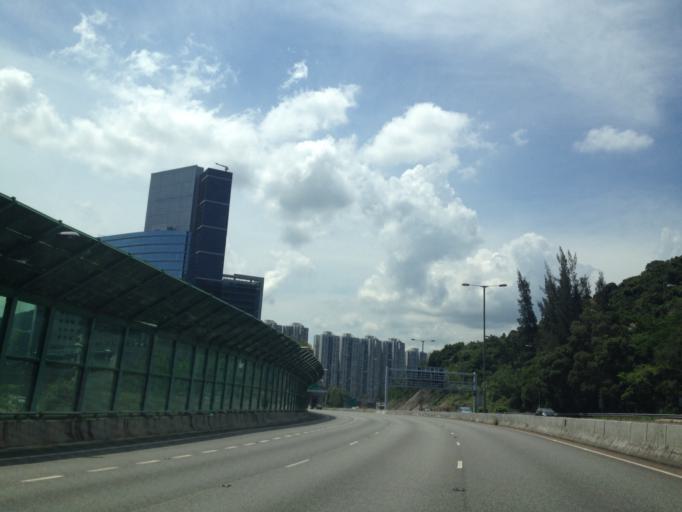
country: HK
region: Sha Tin
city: Sha Tin
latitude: 22.3880
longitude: 114.2111
